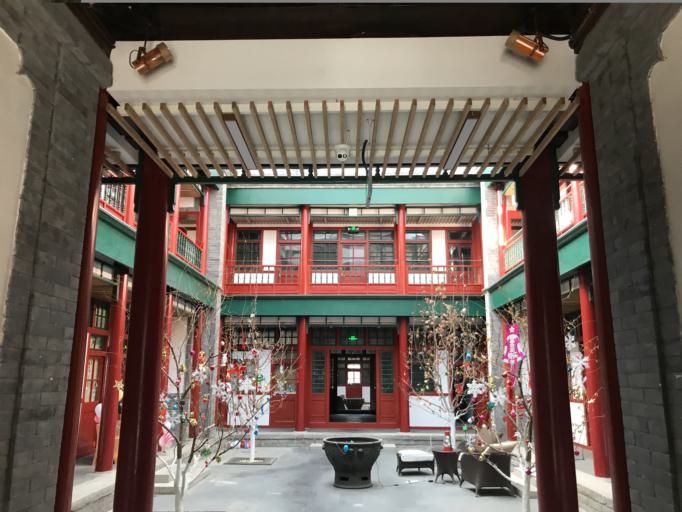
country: CN
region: Beijing
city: Beijing
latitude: 39.8909
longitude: 116.3917
